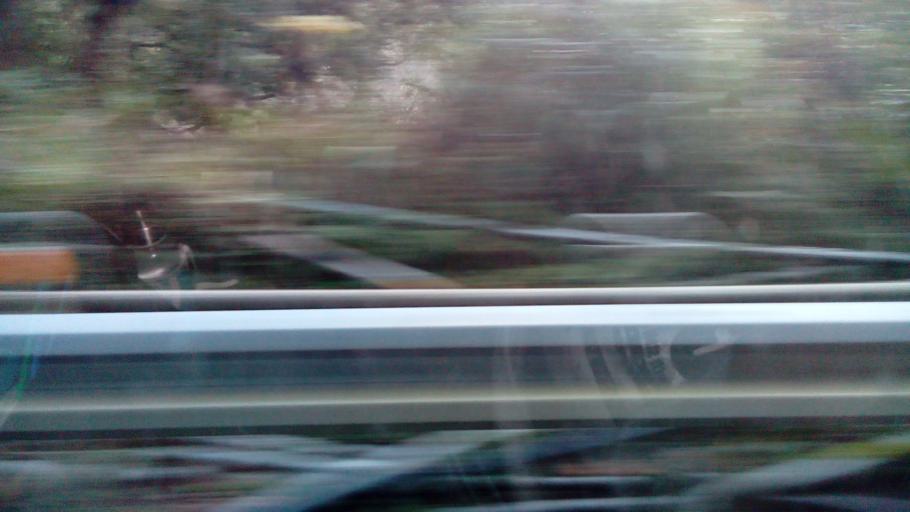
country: TW
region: Taiwan
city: Daxi
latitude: 24.4065
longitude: 121.3565
